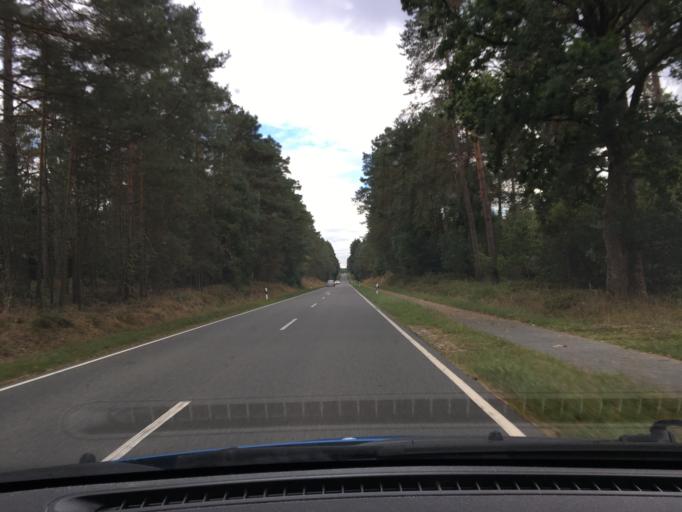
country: DE
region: Lower Saxony
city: Jesteburg
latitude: 53.2553
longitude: 9.9143
